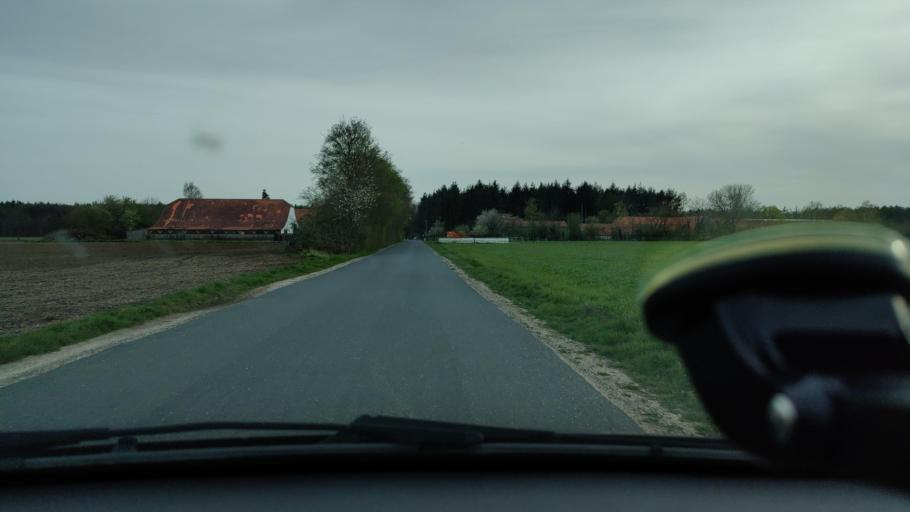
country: DE
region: North Rhine-Westphalia
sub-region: Regierungsbezirk Dusseldorf
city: Kleve
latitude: 51.7430
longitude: 6.1518
